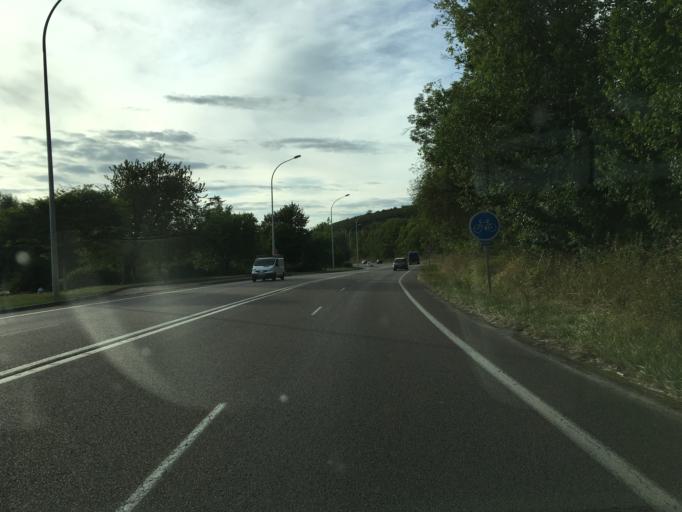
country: FR
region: Bourgogne
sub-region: Departement de la Cote-d'Or
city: Talant
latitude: 47.3282
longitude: 5.0036
